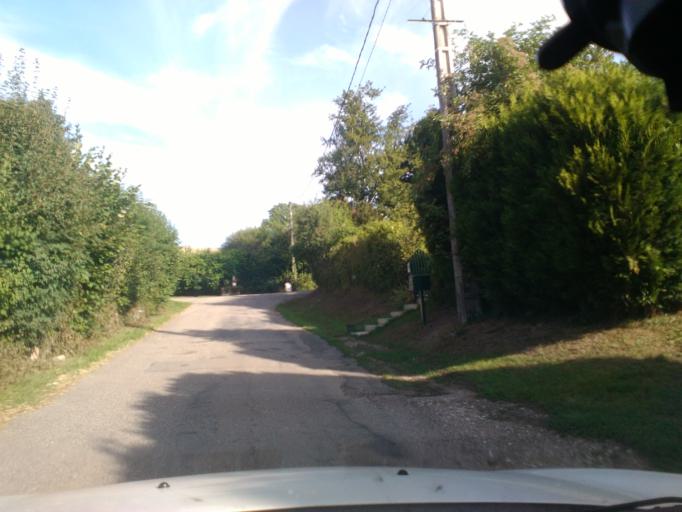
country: FR
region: Lorraine
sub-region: Departement des Vosges
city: Mirecourt
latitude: 48.2793
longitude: 6.0396
